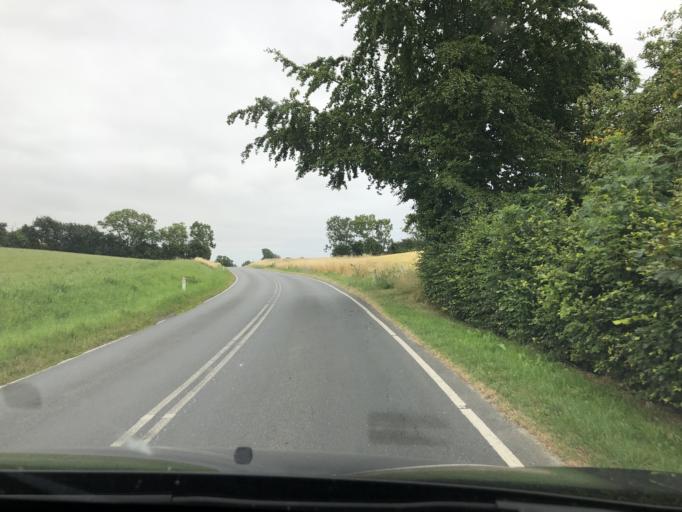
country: DK
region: South Denmark
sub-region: AEro Kommune
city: AEroskobing
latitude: 54.9086
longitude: 10.2900
